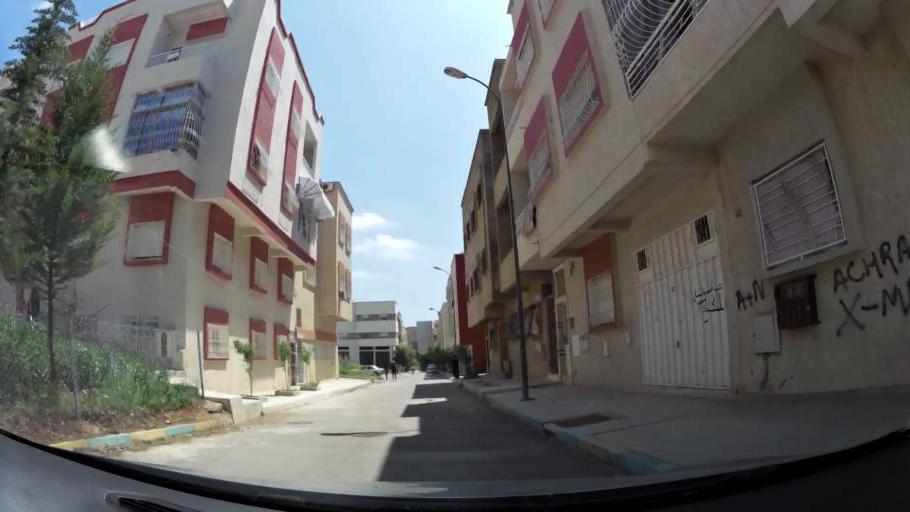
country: MA
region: Fes-Boulemane
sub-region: Fes
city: Fes
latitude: 34.0605
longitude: -5.0305
